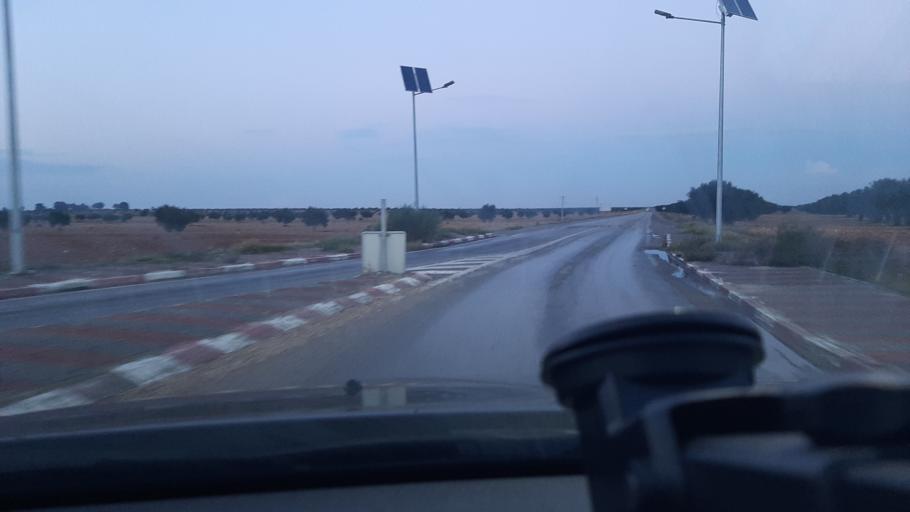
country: TN
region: Al Mahdiyah
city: Shurban
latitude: 35.0397
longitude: 10.5253
